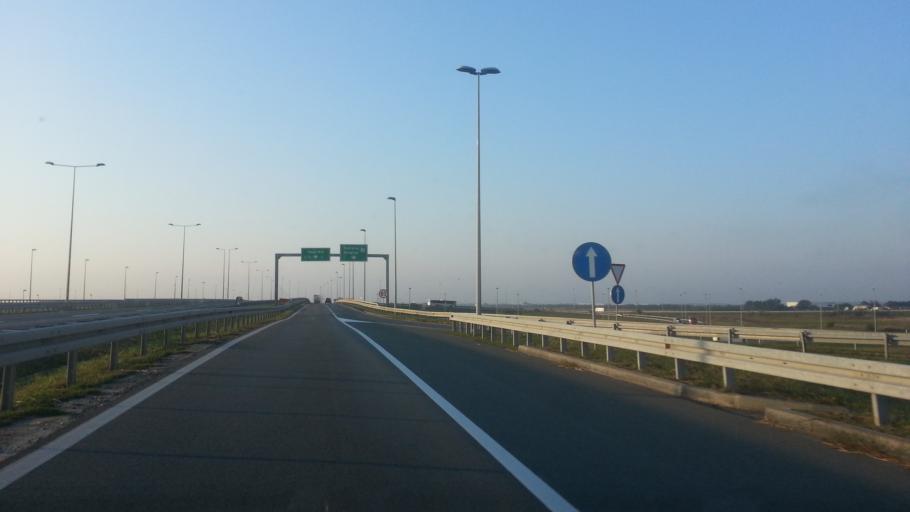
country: RS
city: Dobanovci
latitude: 44.8379
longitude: 20.2503
